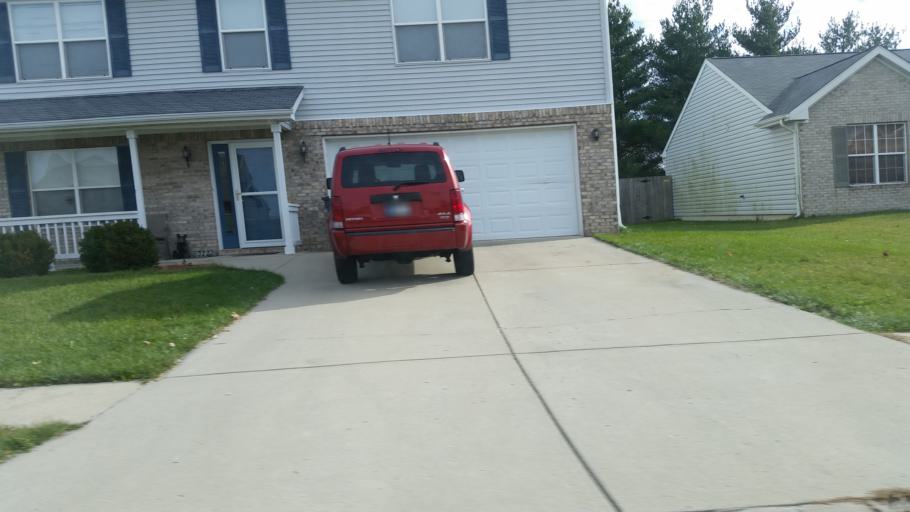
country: US
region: Indiana
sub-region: Howard County
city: Indian Heights
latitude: 40.4461
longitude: -86.1583
